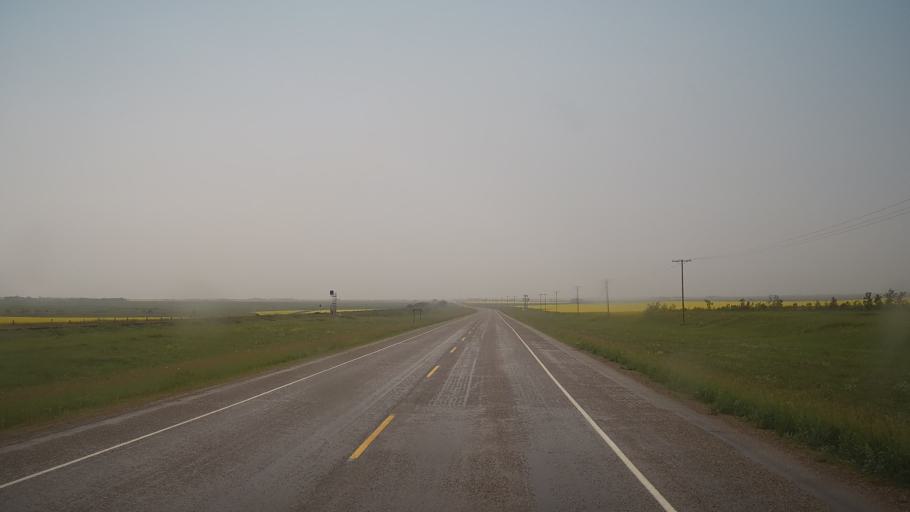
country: CA
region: Saskatchewan
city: Biggar
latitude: 52.1423
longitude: -108.1939
